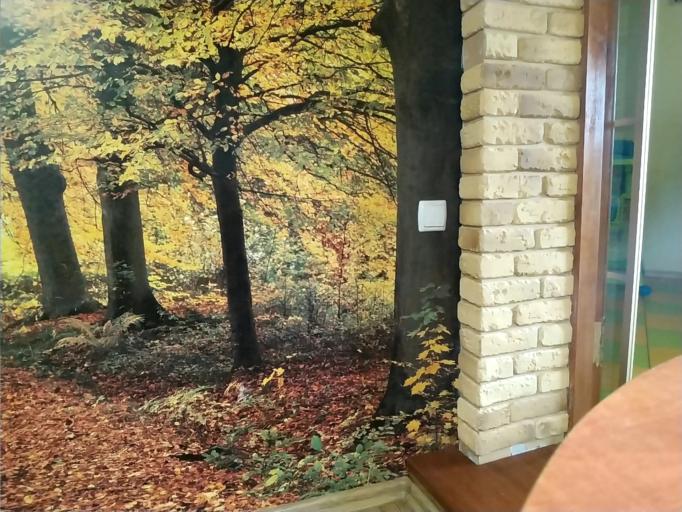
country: RU
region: Smolensk
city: Dorogobuzh
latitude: 54.8608
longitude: 33.3149
